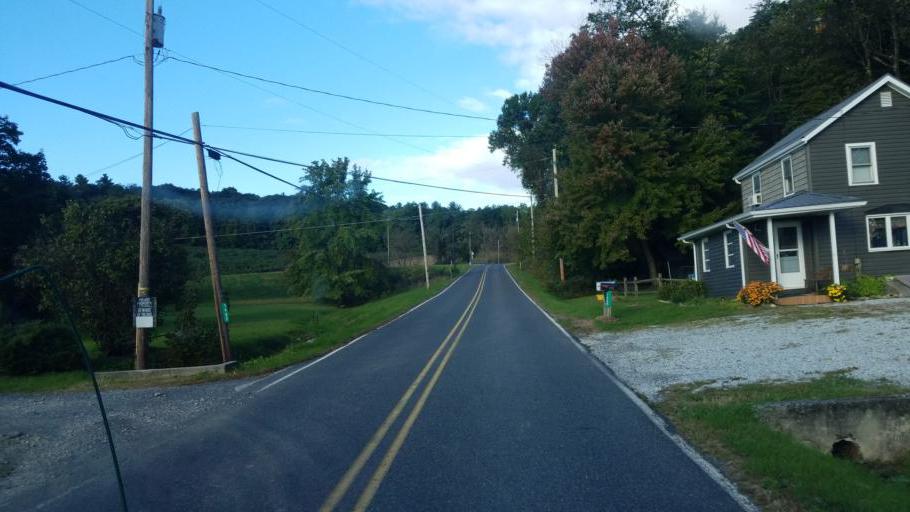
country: US
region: Pennsylvania
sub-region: Adams County
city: Biglerville
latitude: 39.8848
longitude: -77.3624
